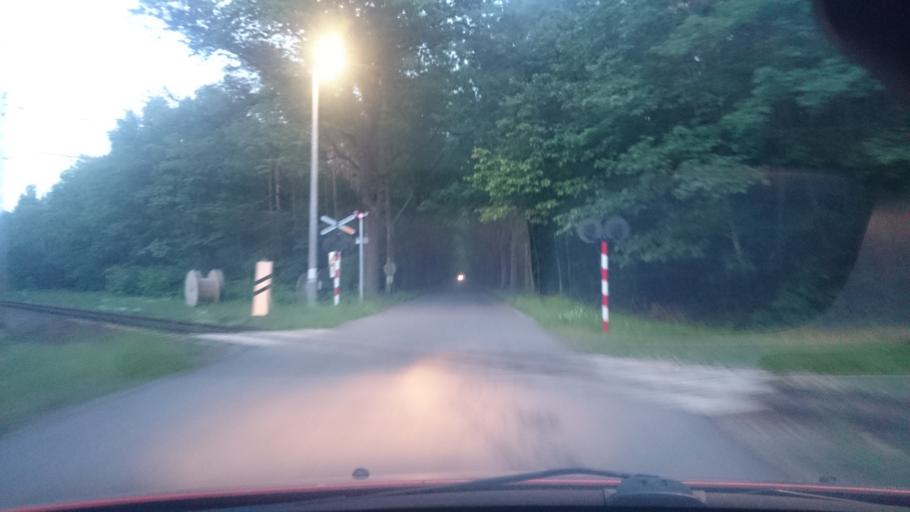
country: PL
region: Opole Voivodeship
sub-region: Powiat opolski
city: Ozimek
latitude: 50.6687
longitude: 18.1746
